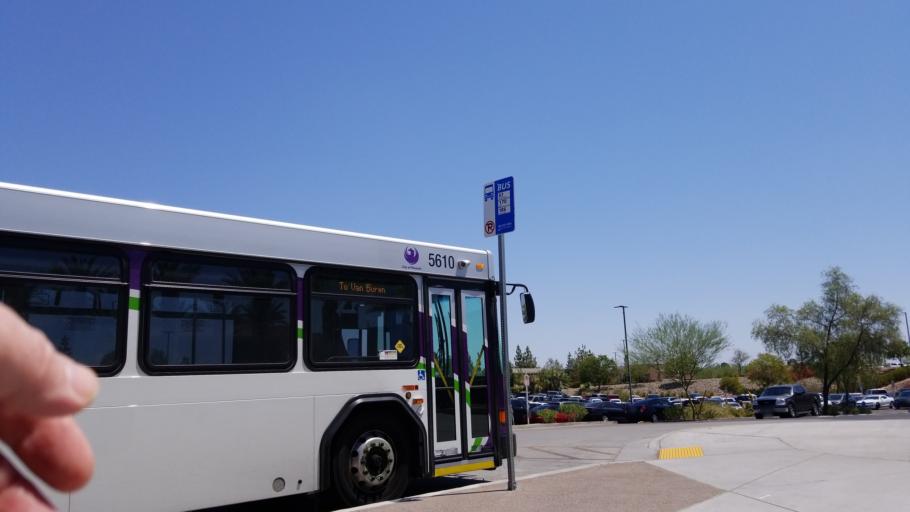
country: US
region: Arizona
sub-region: Maricopa County
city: Peoria
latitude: 33.6431
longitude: -112.2251
